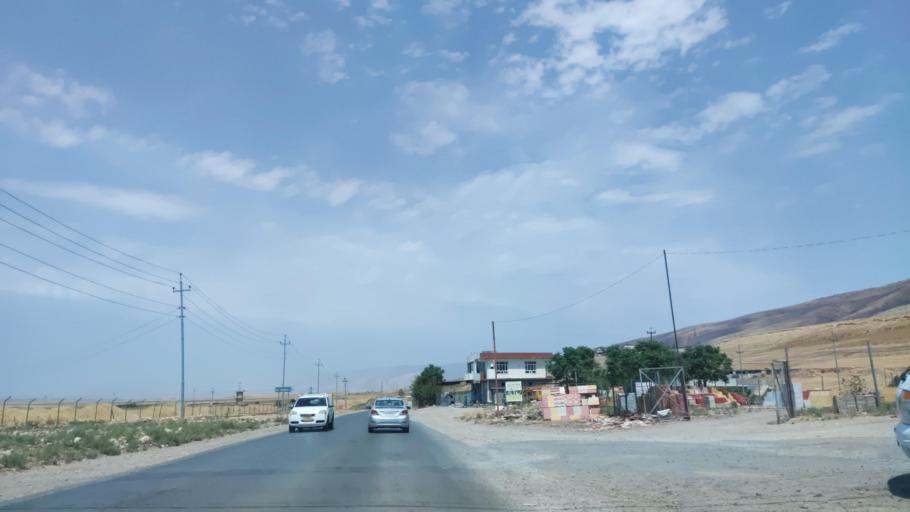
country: IQ
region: Arbil
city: Shaqlawah
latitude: 36.5296
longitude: 44.3589
